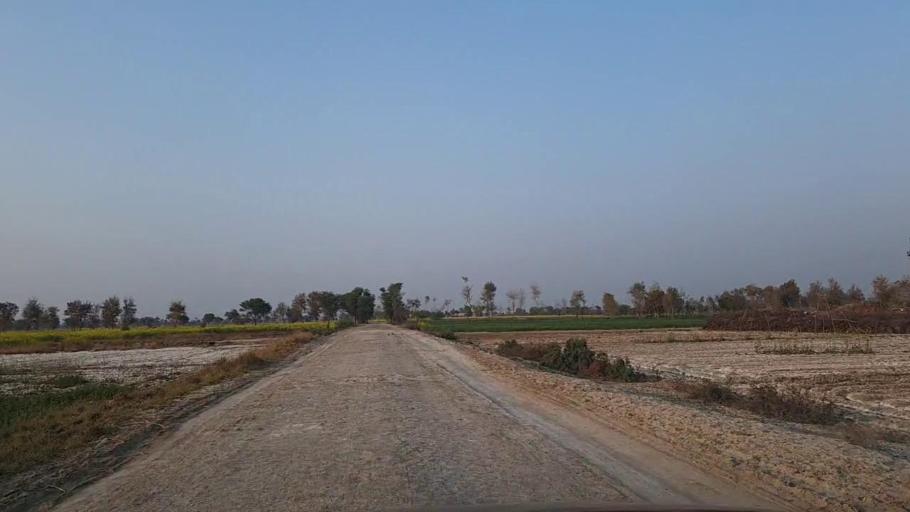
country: PK
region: Sindh
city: Daur
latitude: 26.4283
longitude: 68.3859
